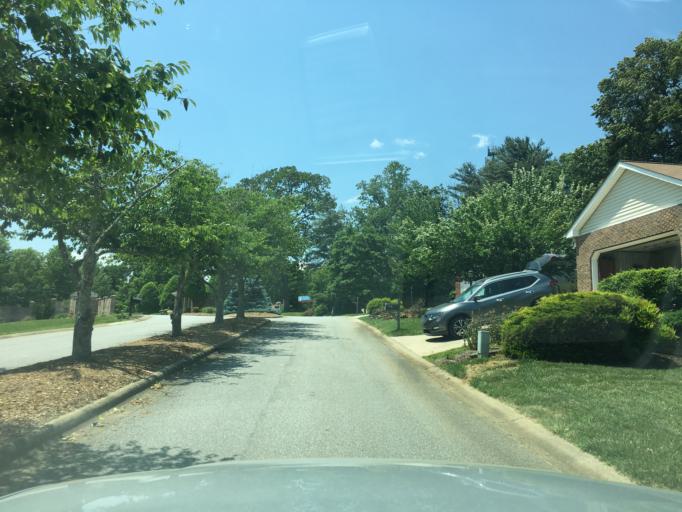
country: US
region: North Carolina
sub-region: Buncombe County
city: Biltmore Forest
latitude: 35.5107
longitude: -82.5175
